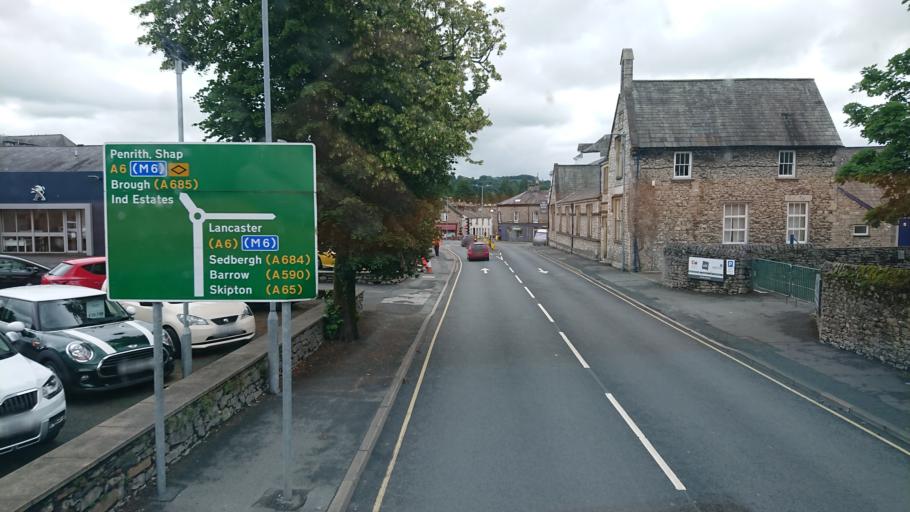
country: GB
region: England
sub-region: Cumbria
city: Kendal
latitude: 54.3317
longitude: -2.7415
